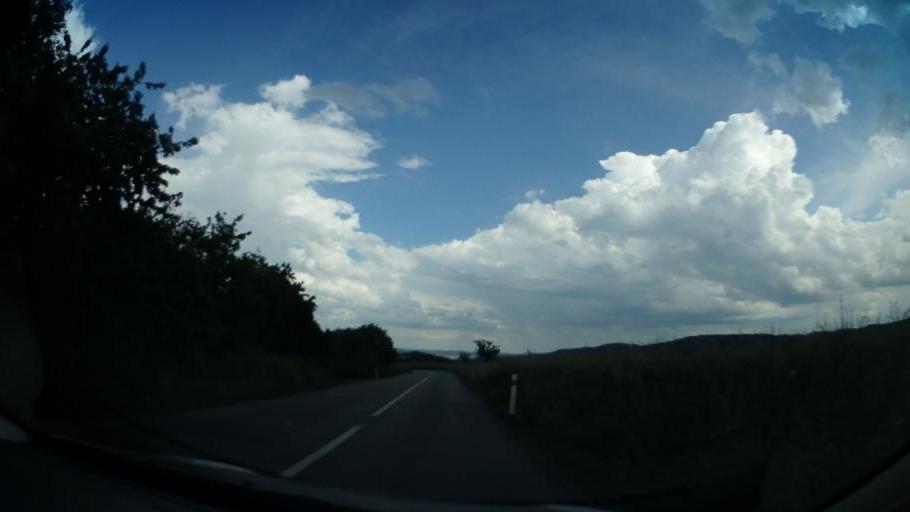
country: CZ
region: South Moravian
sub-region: Okres Brno-Venkov
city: Dolni Loucky
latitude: 49.3801
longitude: 16.3461
